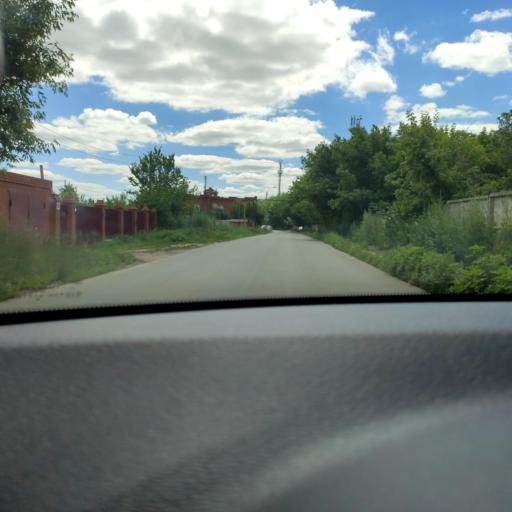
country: RU
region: Samara
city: Smyshlyayevka
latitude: 53.2120
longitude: 50.3277
